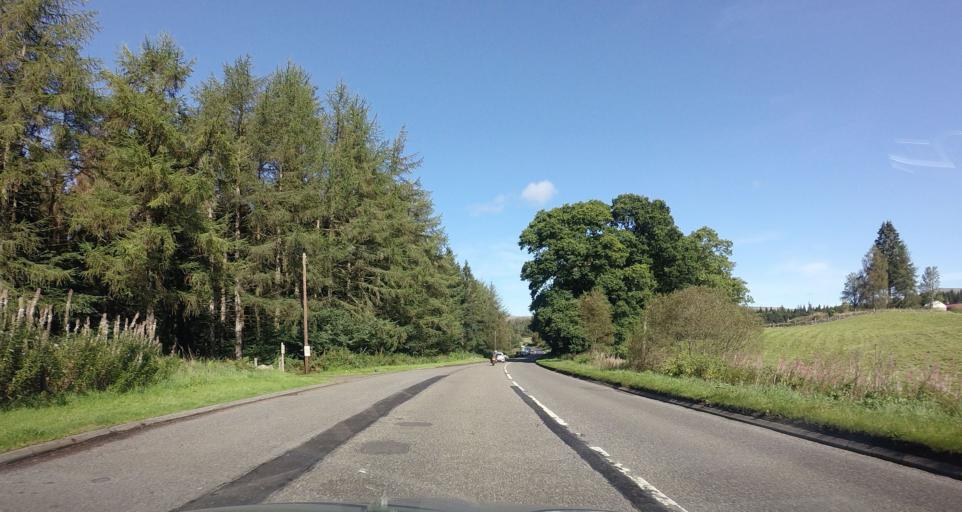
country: GB
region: Scotland
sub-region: Stirling
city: Callander
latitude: 56.2190
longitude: -4.1625
